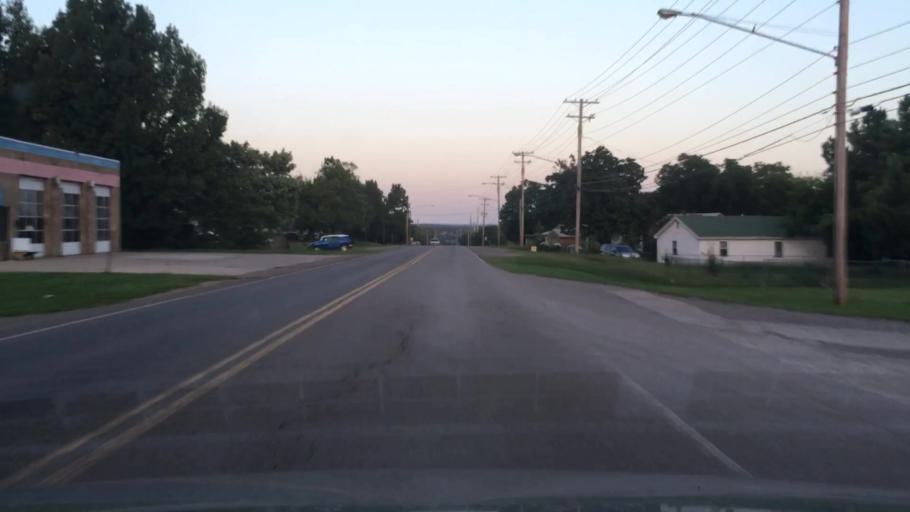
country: US
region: Oklahoma
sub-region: Cherokee County
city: Tahlequah
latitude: 35.9147
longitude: -94.9833
